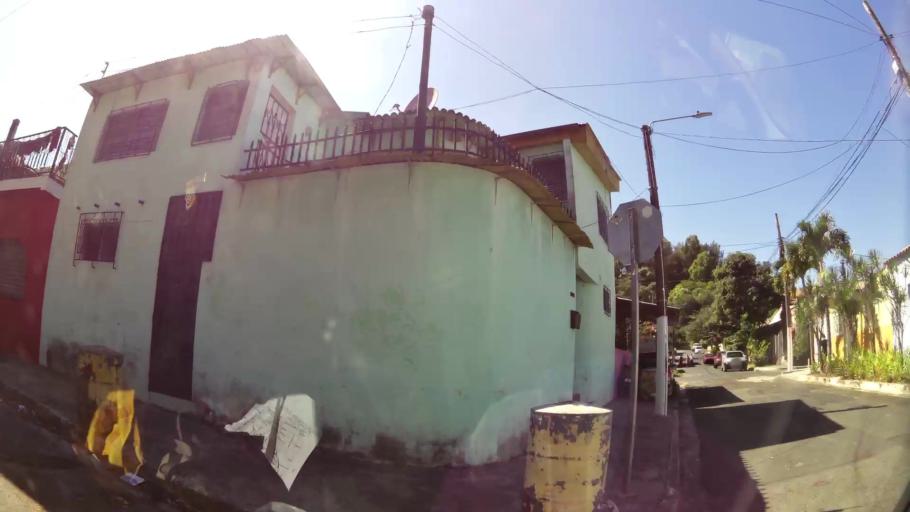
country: SV
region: La Libertad
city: Santa Tecla
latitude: 13.6717
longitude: -89.3015
